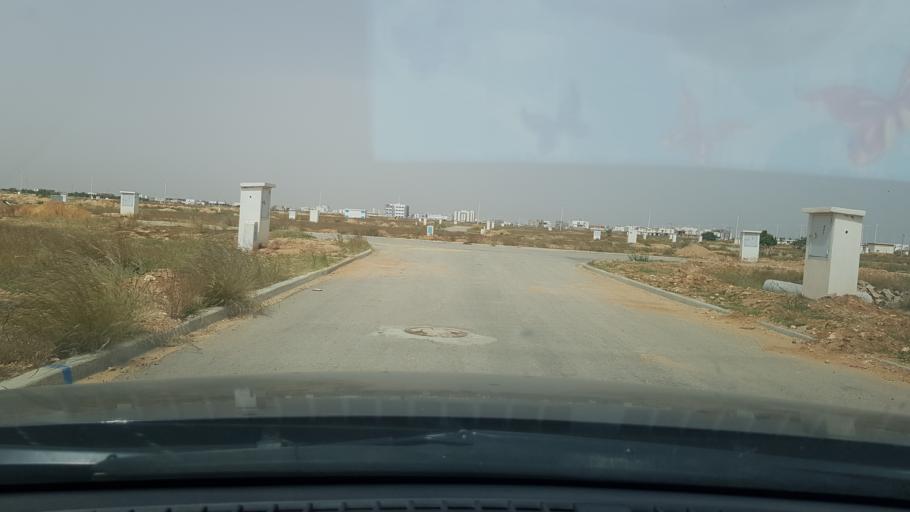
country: TN
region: Safaqis
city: Al Qarmadah
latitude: 34.8269
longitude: 10.7417
